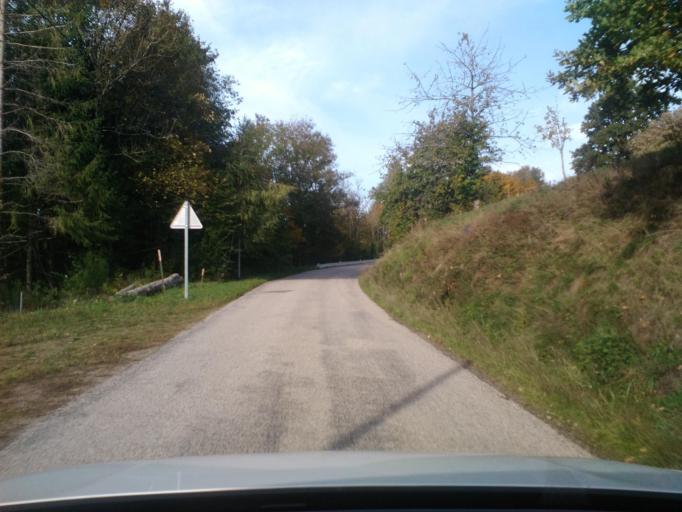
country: FR
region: Lorraine
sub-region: Departement des Vosges
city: Senones
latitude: 48.3619
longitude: 7.0344
